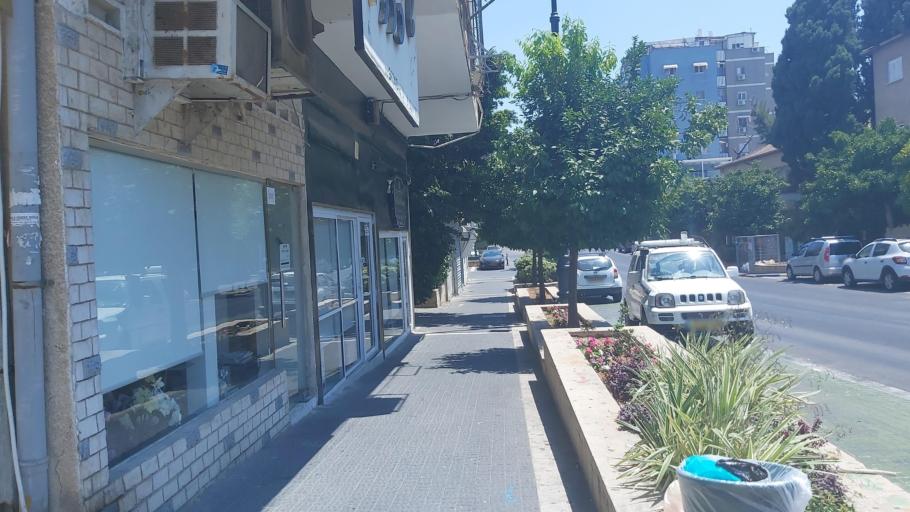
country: IL
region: Central District
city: Rishon LeZiyyon
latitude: 31.9635
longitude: 34.8077
